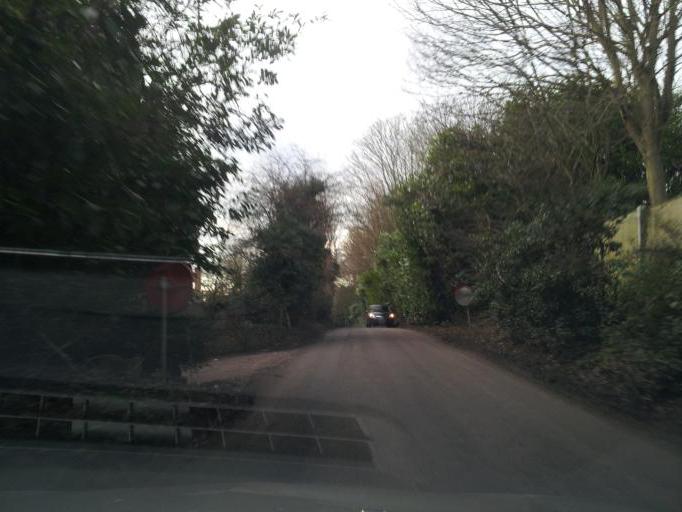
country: GB
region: England
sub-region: Norfolk
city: Surlingham
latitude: 52.6247
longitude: 1.4130
